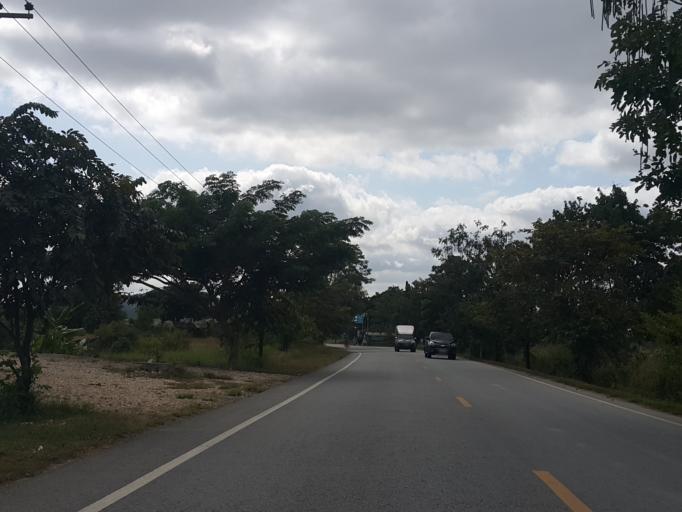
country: TH
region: Lamphun
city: Ban Thi
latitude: 18.6399
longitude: 99.1060
